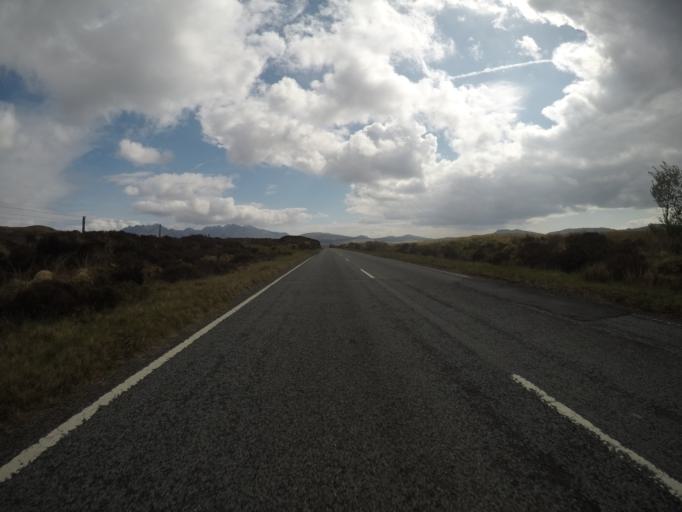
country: GB
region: Scotland
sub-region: Highland
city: Isle of Skye
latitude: 57.3140
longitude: -6.3198
